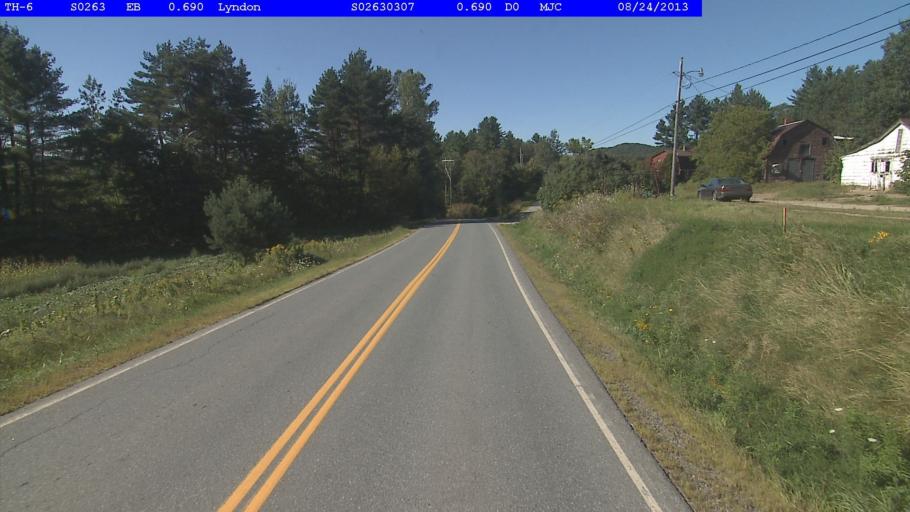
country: US
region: Vermont
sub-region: Caledonia County
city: Lyndon
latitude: 44.4990
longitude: -71.9805
